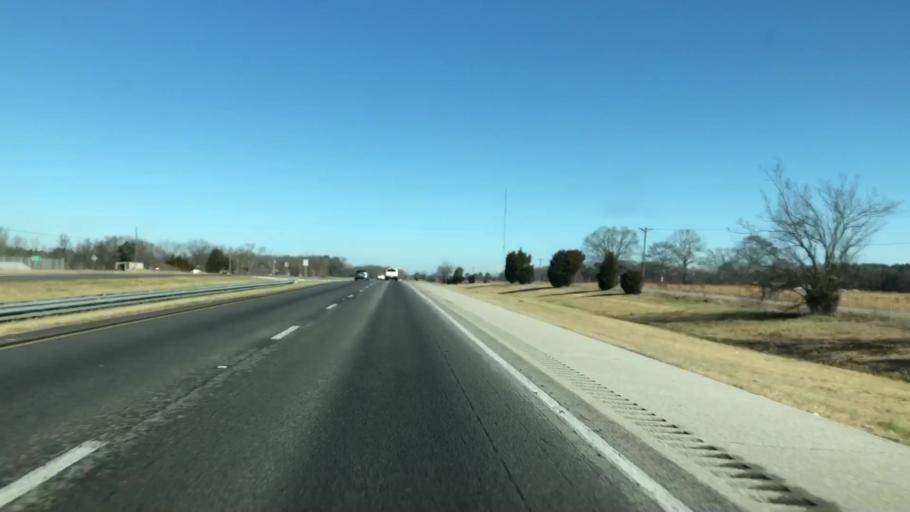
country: US
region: Alabama
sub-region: Limestone County
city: Athens
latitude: 34.8775
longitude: -86.9204
